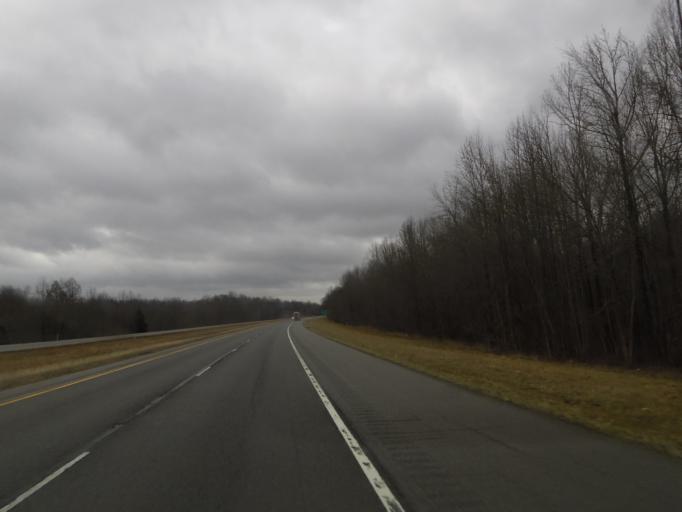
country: US
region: Illinois
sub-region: Johnson County
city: Vienna
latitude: 37.3210
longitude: -88.7621
